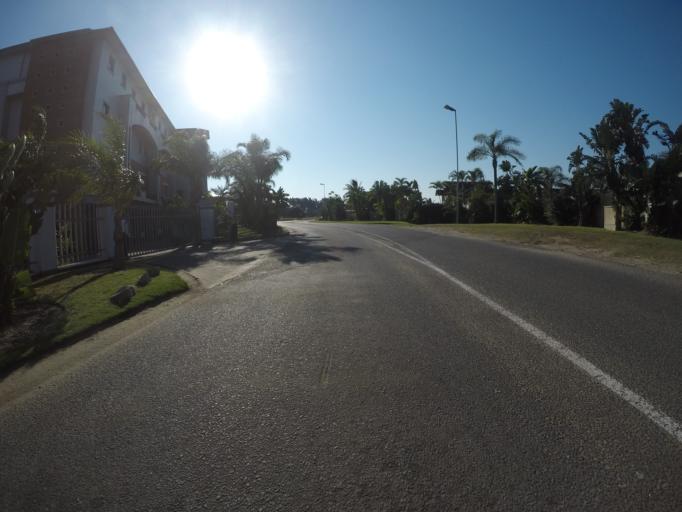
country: ZA
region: KwaZulu-Natal
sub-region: uThungulu District Municipality
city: Richards Bay
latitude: -28.7937
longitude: 32.0815
